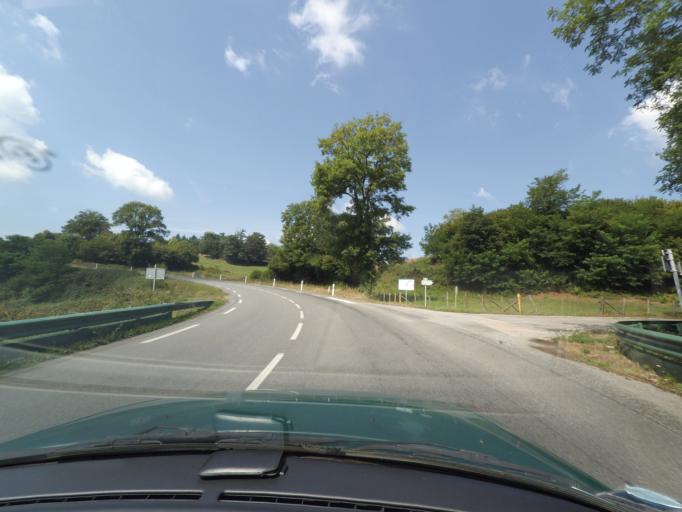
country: FR
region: Limousin
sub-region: Departement de la Haute-Vienne
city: Linards
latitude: 45.7677
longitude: 1.5534
